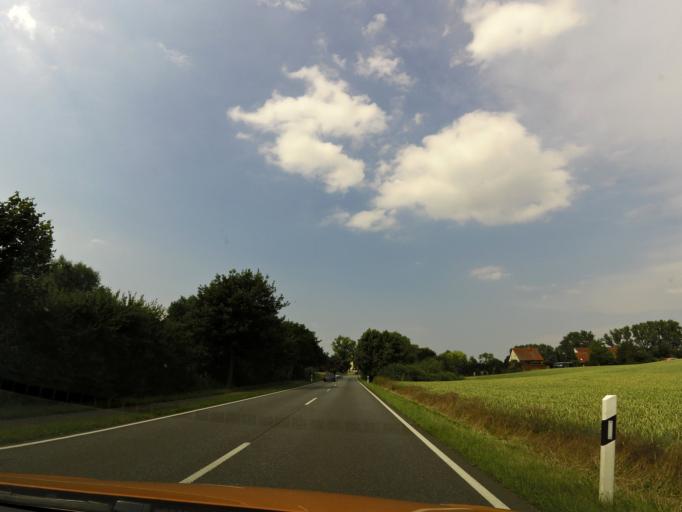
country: DE
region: Mecklenburg-Vorpommern
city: Krakow am See
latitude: 53.6821
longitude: 12.2678
